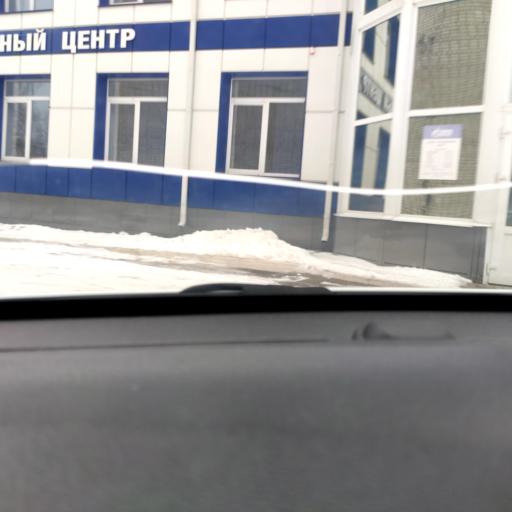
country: RU
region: Voronezj
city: Somovo
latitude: 51.7461
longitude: 39.3586
